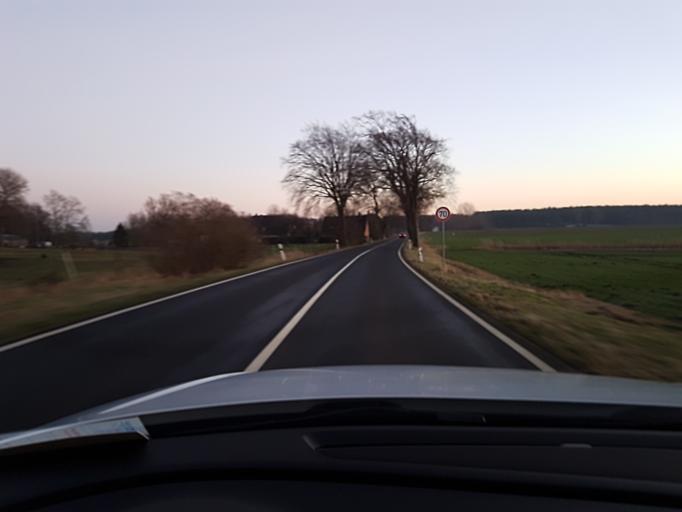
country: DE
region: Mecklenburg-Vorpommern
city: Gingst
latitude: 54.5143
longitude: 13.2689
